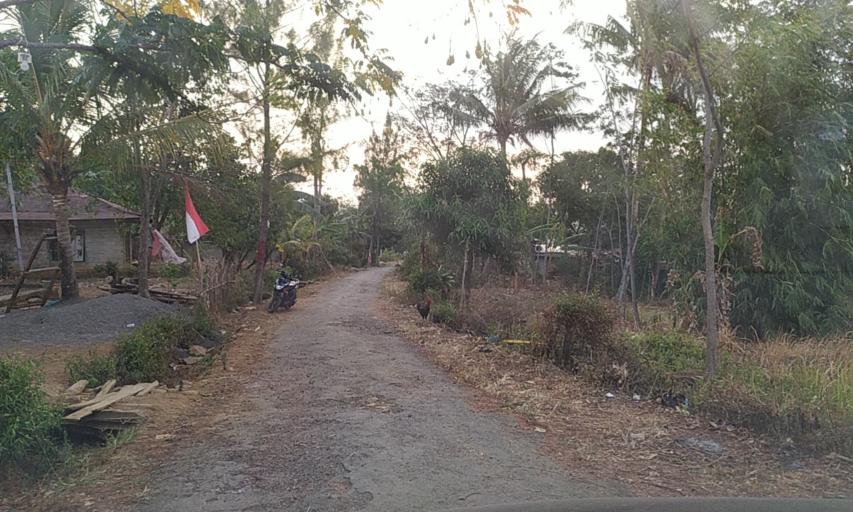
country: ID
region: Central Java
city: Randudongkal
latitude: -7.1328
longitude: 109.3629
